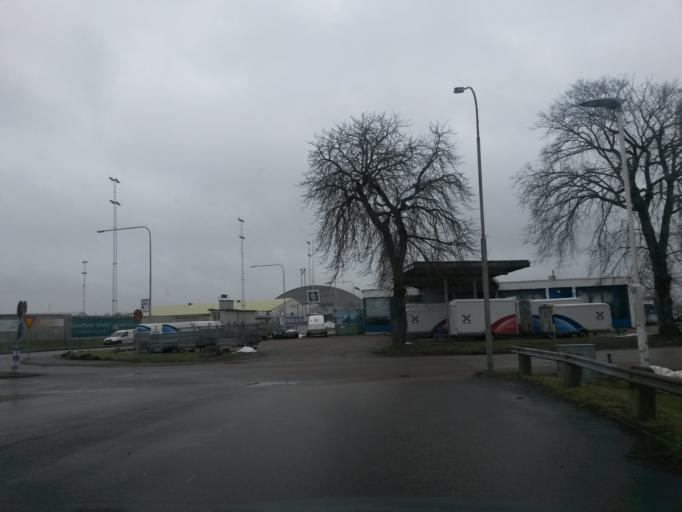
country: SE
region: Vaestra Goetaland
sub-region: Vanersborgs Kommun
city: Vanersborg
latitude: 58.3658
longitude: 12.3222
